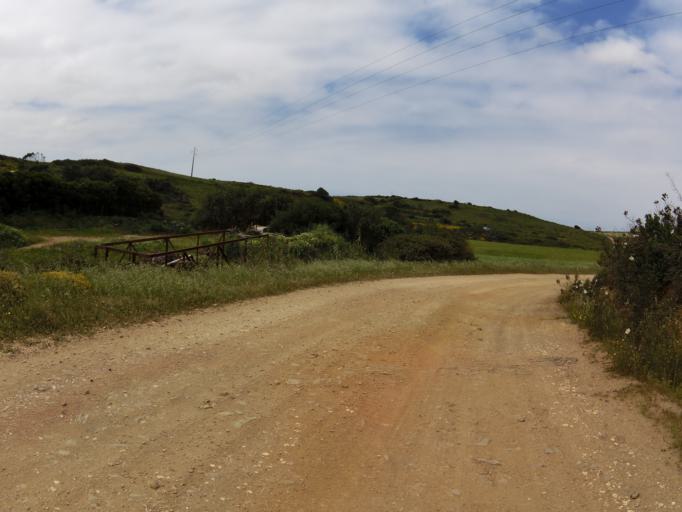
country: PT
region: Faro
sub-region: Vila do Bispo
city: Vila do Bispo
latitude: 37.0862
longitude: -8.8956
